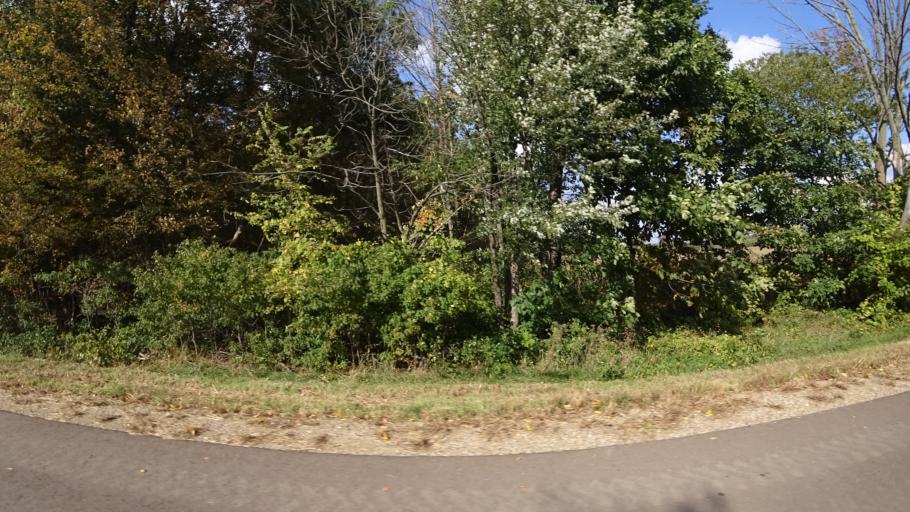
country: US
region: Michigan
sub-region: Calhoun County
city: Athens
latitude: 42.0609
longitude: -85.2104
